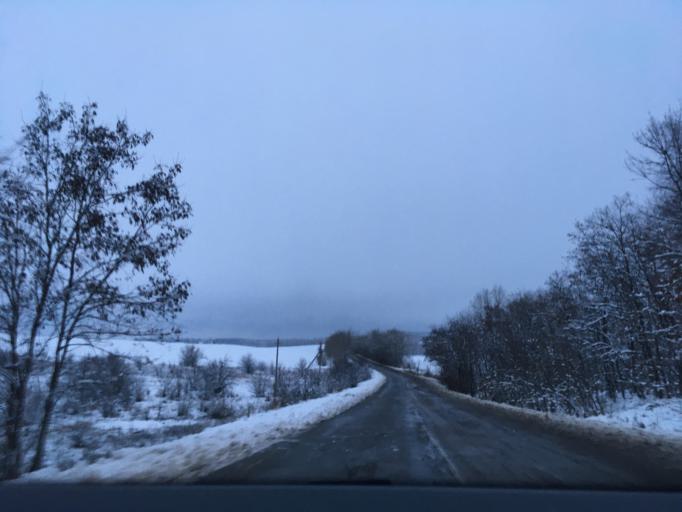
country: RU
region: Voronezj
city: Verkhniy Mamon
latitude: 50.0529
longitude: 40.2490
